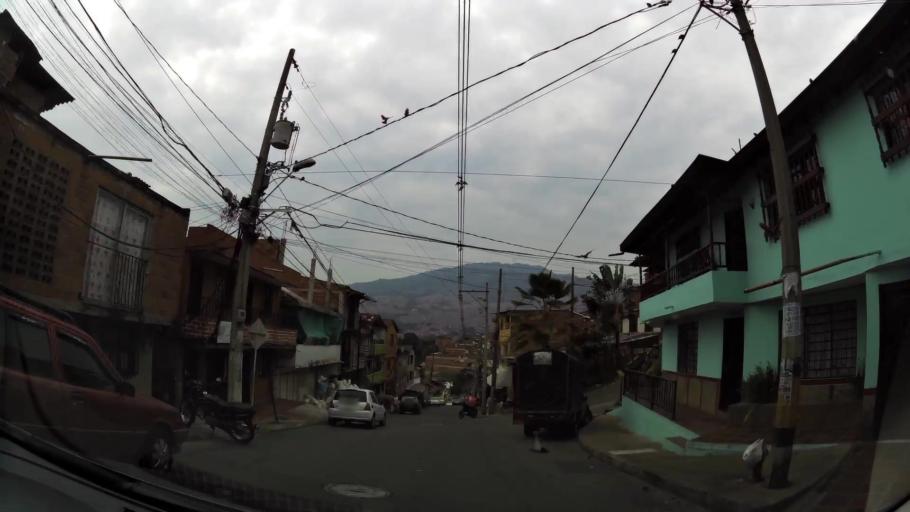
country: CO
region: Antioquia
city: Medellin
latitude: 6.2768
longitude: -75.5624
